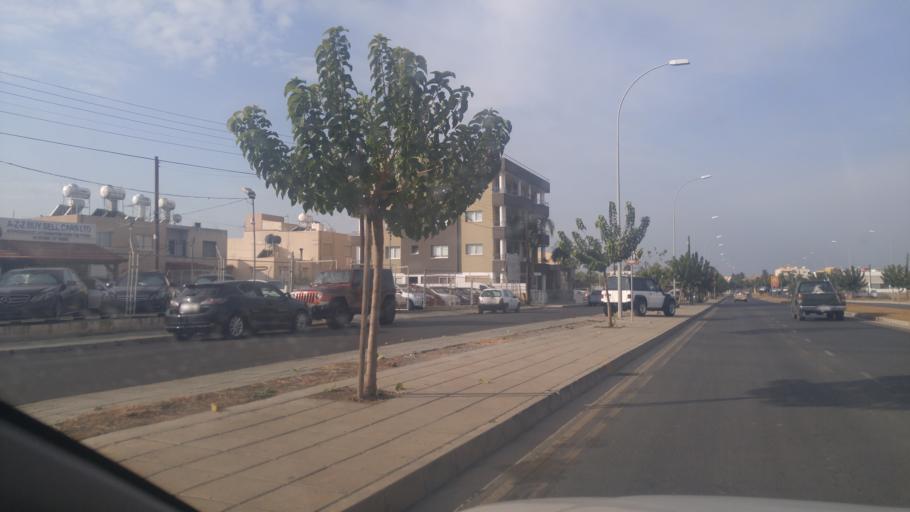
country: CY
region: Limassol
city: Pano Polemidia
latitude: 34.6779
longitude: 33.0025
